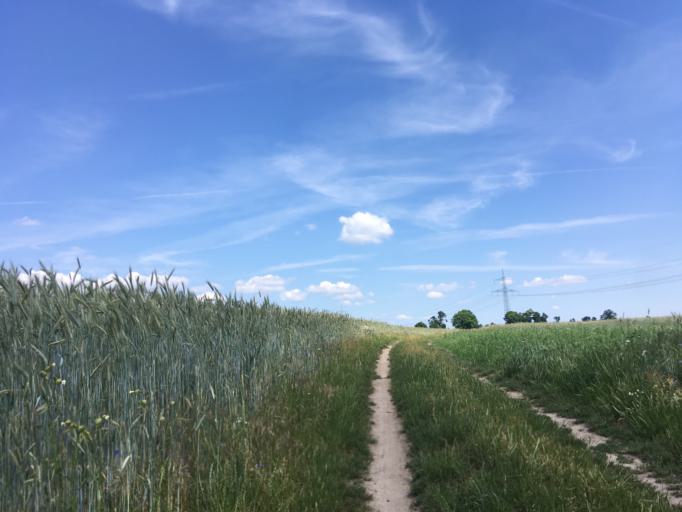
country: DE
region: Brandenburg
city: Neuenhagen
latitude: 52.5452
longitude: 13.6706
